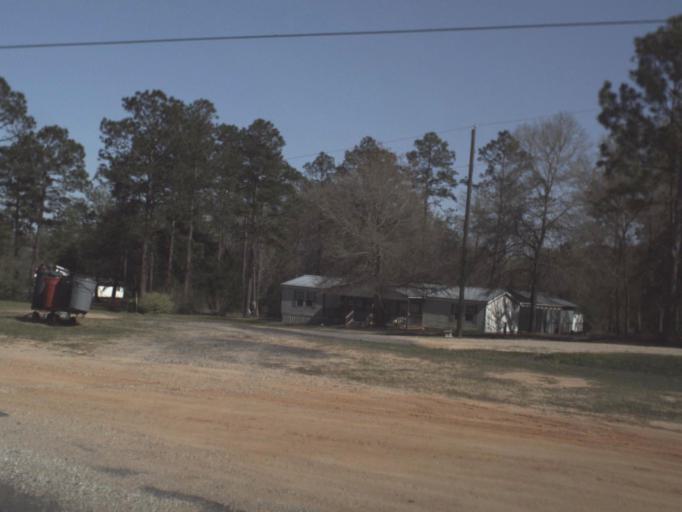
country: US
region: Florida
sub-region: Walton County
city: DeFuniak Springs
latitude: 30.7314
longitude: -85.9225
